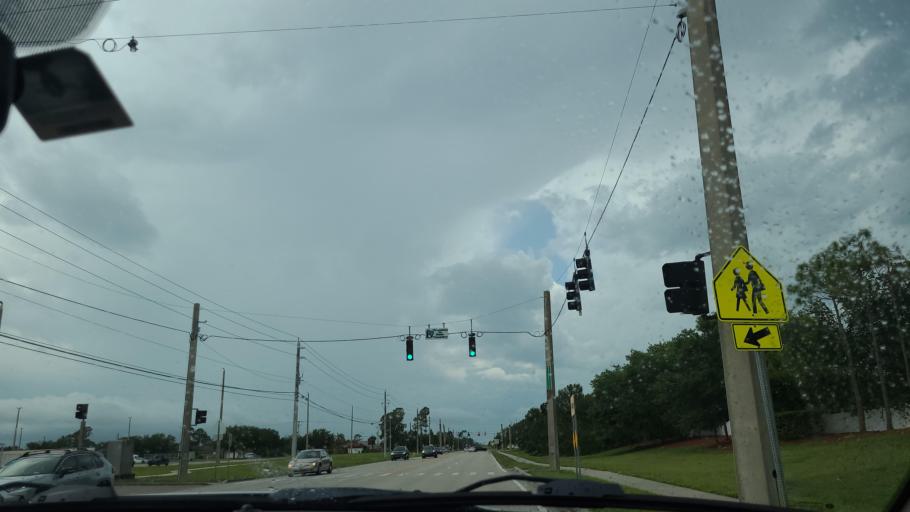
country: US
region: Florida
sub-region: Brevard County
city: Grant-Valkaria
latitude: 27.9529
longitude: -80.6749
